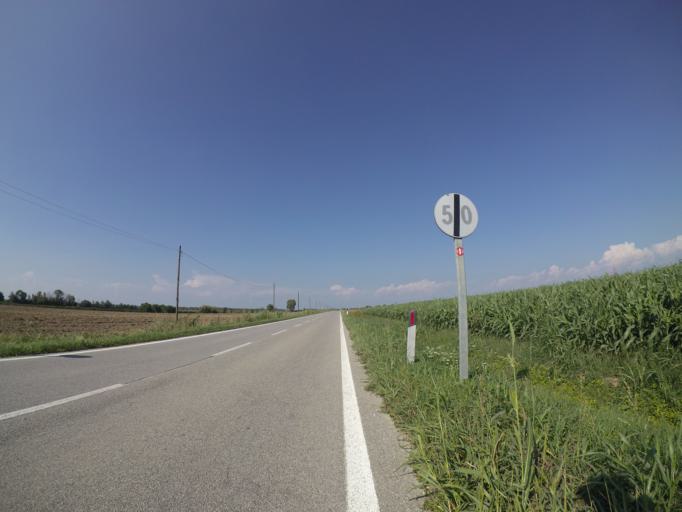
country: IT
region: Friuli Venezia Giulia
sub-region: Provincia di Udine
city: Marano Lagunare
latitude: 45.7802
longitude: 13.1631
